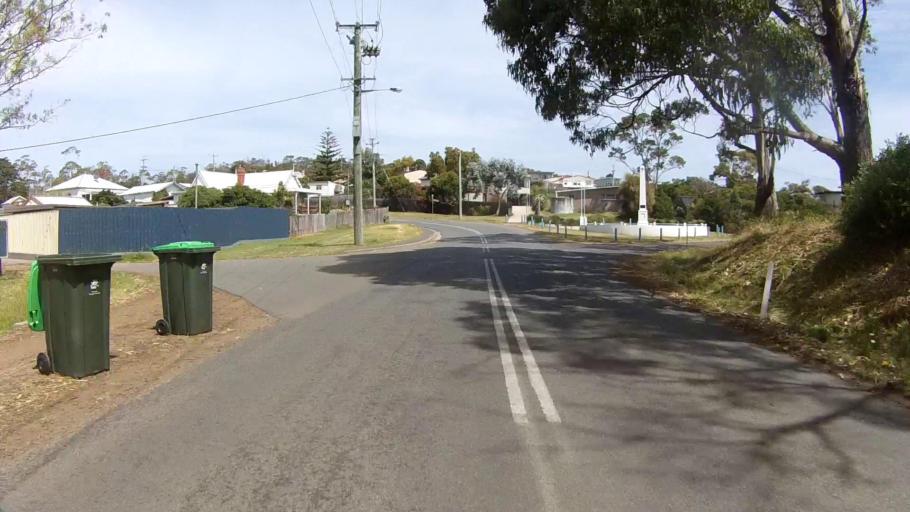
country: AU
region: Tasmania
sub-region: Kingborough
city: Blackmans Bay
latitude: -43.0269
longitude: 147.4168
